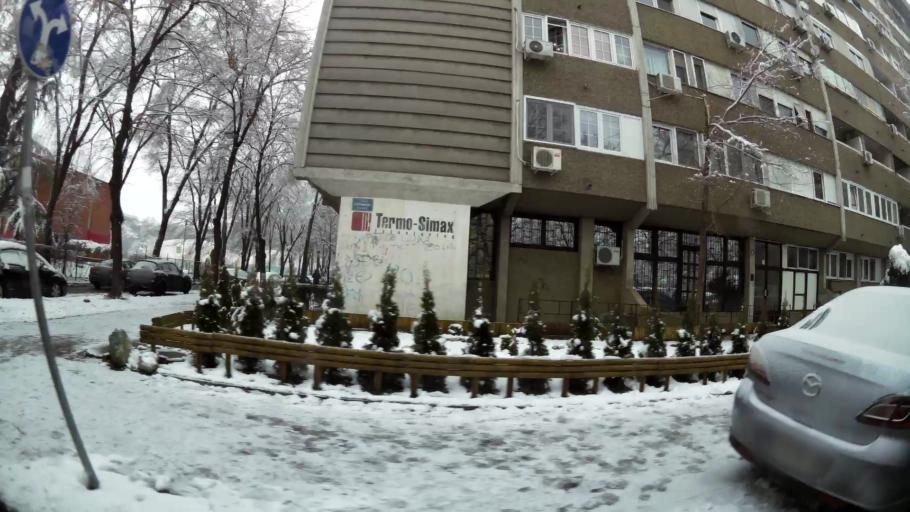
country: RS
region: Central Serbia
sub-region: Belgrade
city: Zemun
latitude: 44.8286
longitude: 20.4170
